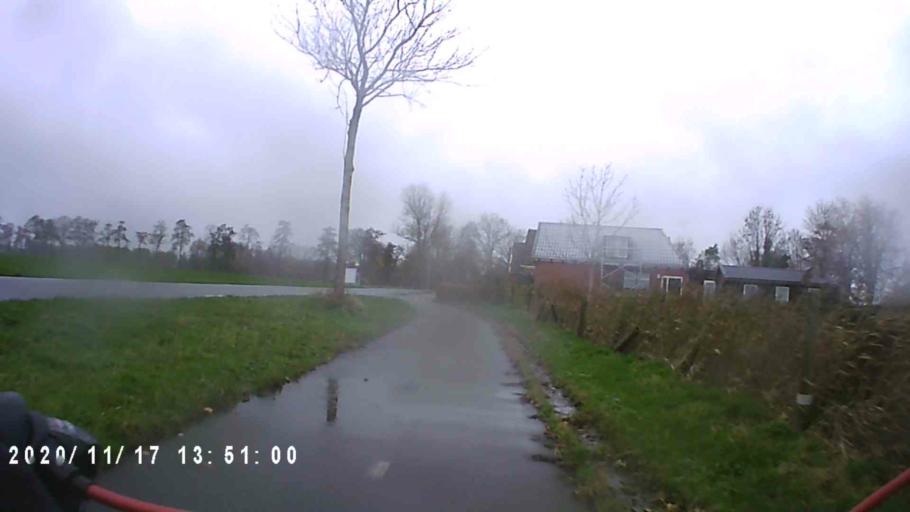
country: NL
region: Groningen
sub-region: Gemeente Zuidhorn
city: Zuidhorn
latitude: 53.2301
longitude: 6.3645
